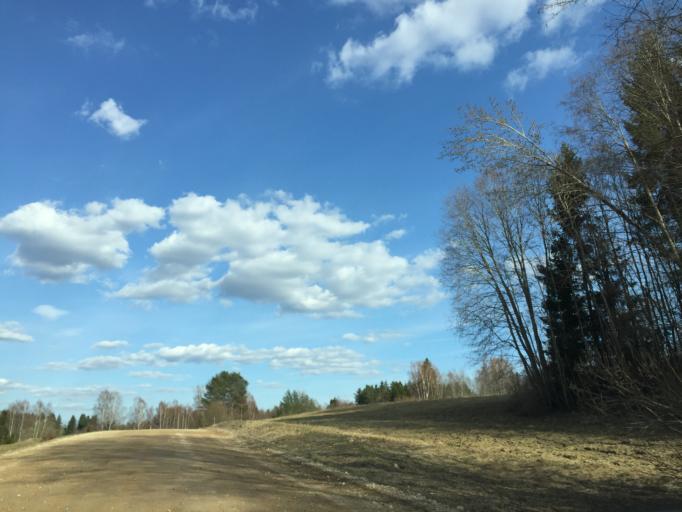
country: EE
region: Tartu
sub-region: Noo vald
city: Noo
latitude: 58.1119
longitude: 26.5444
